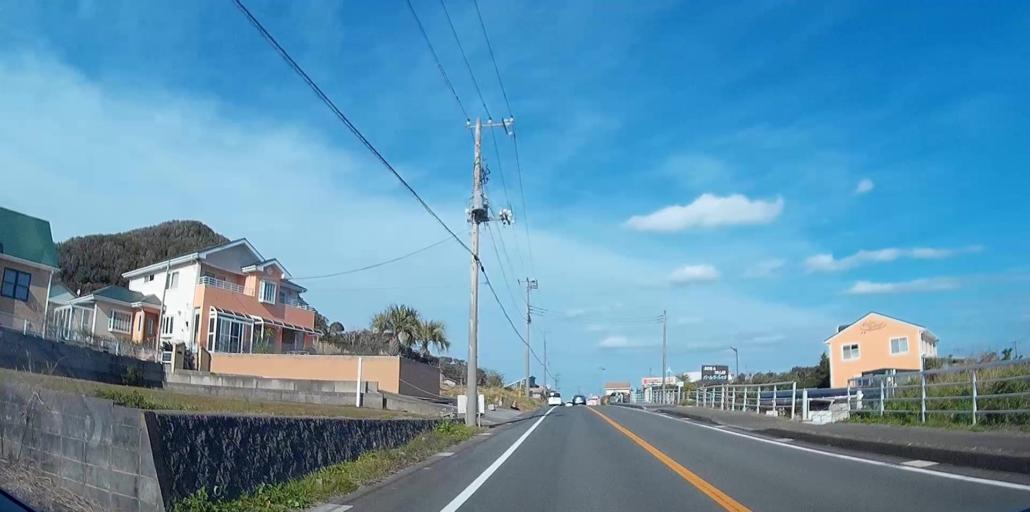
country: JP
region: Chiba
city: Tateyama
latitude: 34.9155
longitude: 139.9340
